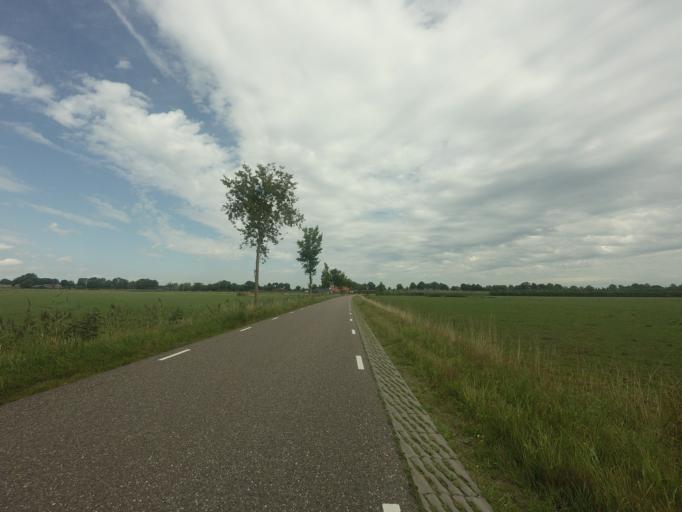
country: NL
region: Overijssel
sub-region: Gemeente Dalfsen
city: Dalfsen
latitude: 52.4726
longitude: 6.3612
